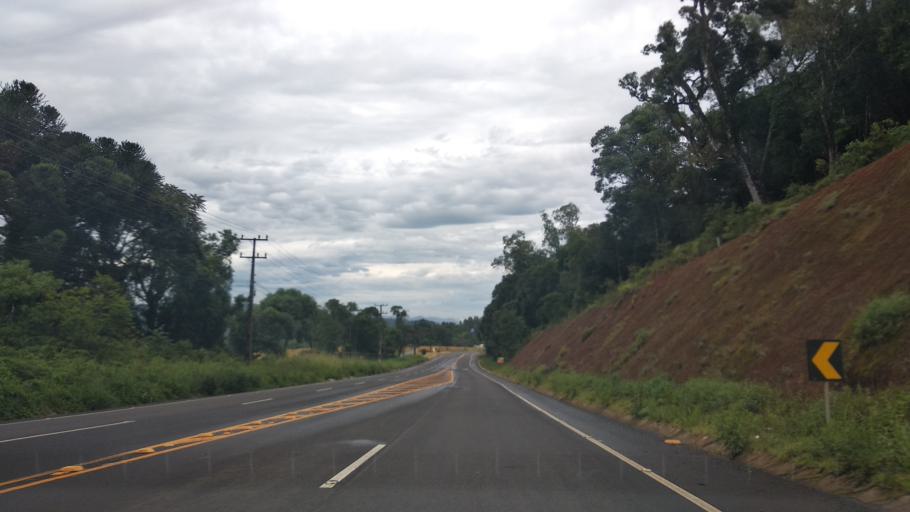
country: BR
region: Santa Catarina
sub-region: Videira
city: Videira
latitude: -27.0520
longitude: -51.1841
